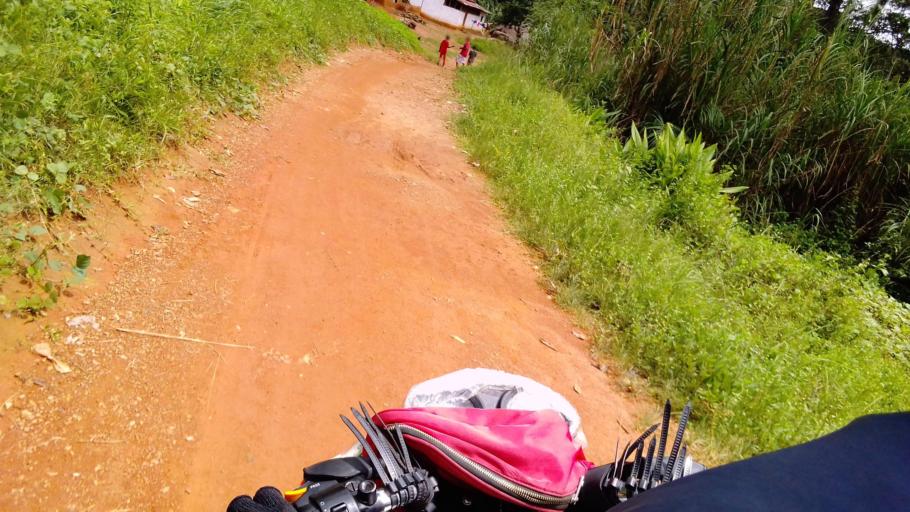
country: SL
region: Eastern Province
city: Koyima
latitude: 8.6781
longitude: -11.0063
